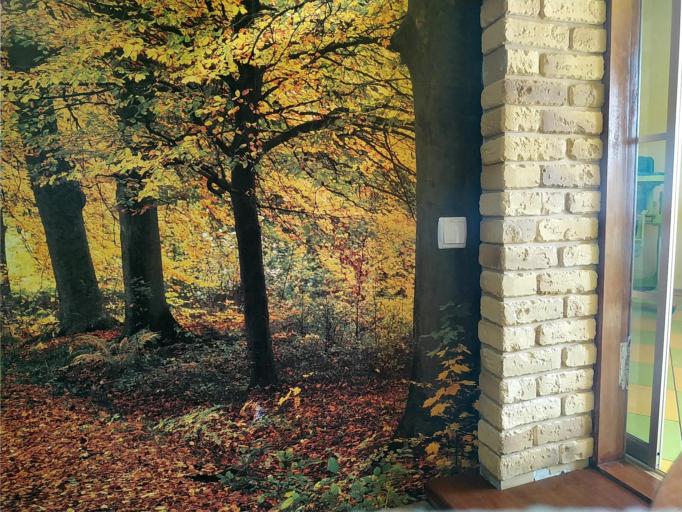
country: RU
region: Smolensk
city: Katyn'
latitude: 54.9997
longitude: 31.7512
